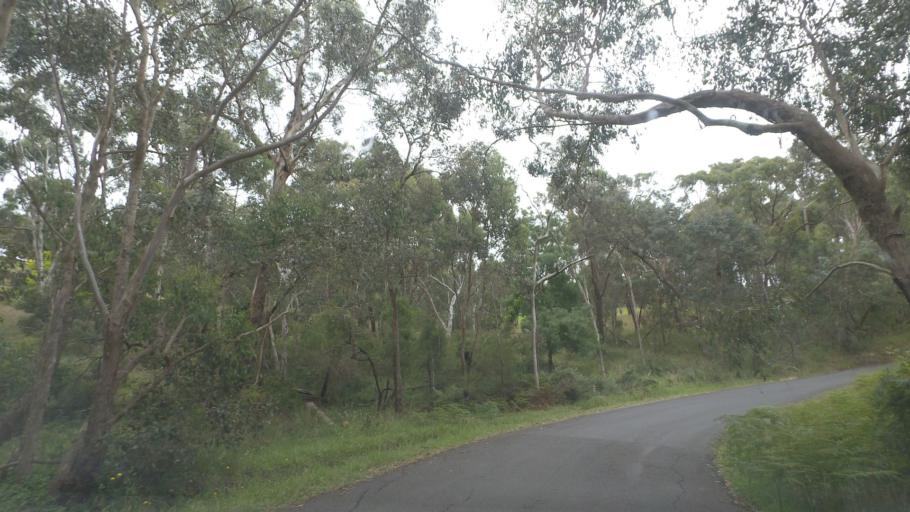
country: AU
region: Victoria
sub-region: Manningham
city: Warrandyte
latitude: -37.7614
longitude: 145.2215
